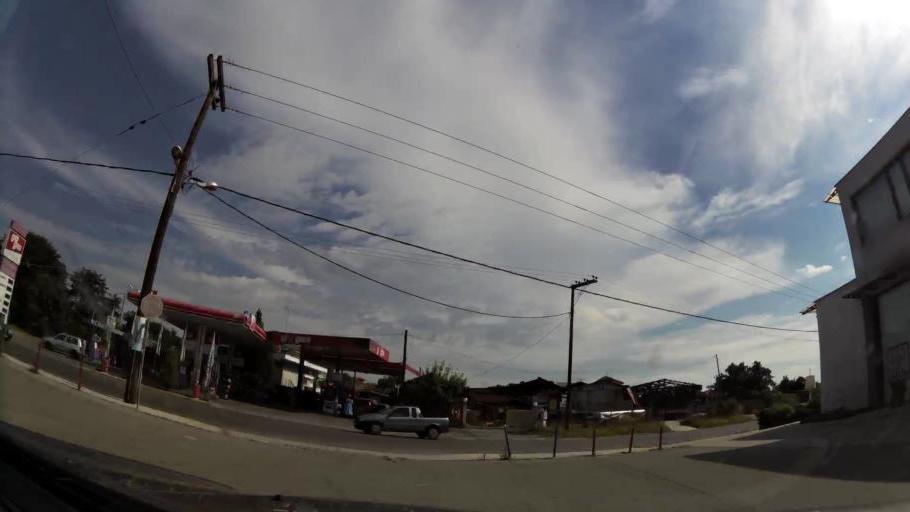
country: GR
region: Central Macedonia
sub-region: Nomos Pierias
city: Katerini
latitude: 40.2829
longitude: 22.5054
